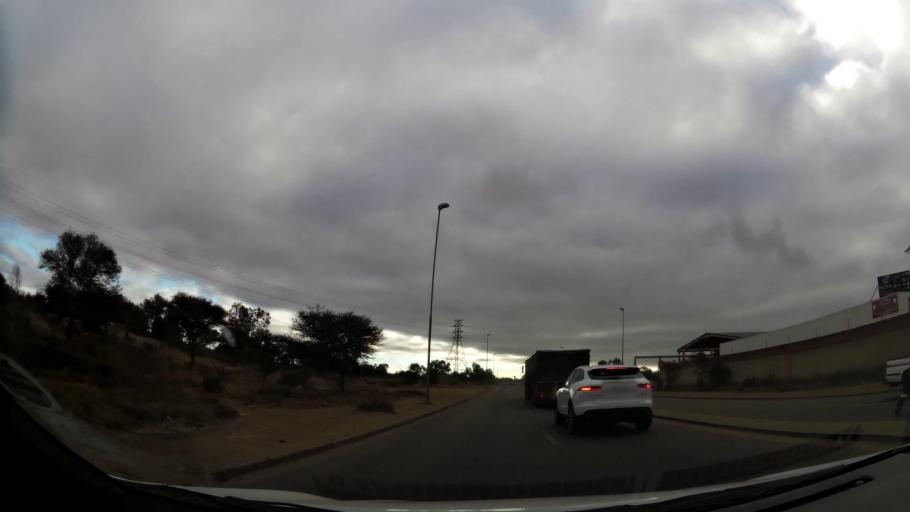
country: ZA
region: Limpopo
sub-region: Capricorn District Municipality
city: Polokwane
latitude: -23.8868
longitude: 29.4302
